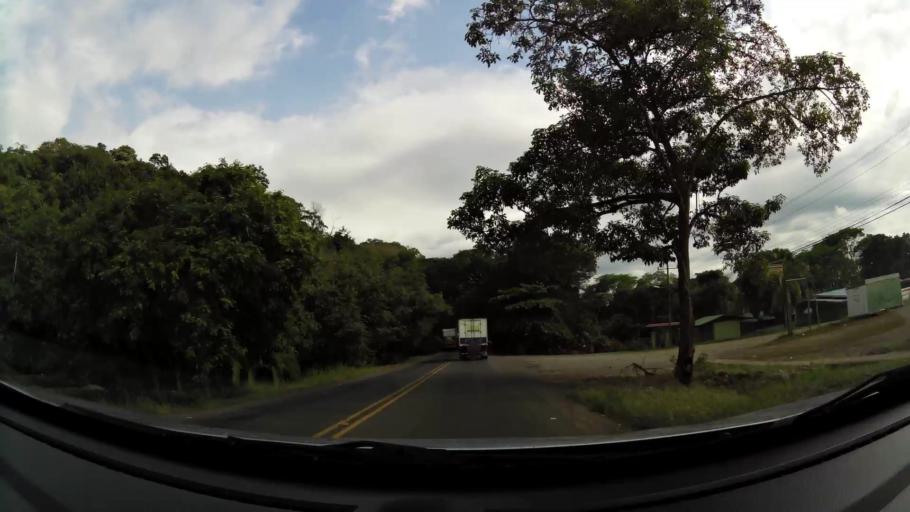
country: CR
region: Guanacaste
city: Juntas
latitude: 10.1806
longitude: -84.9349
